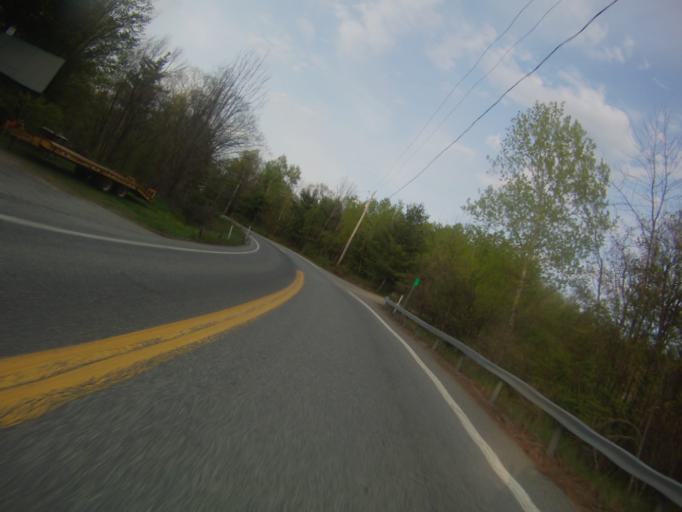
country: US
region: New York
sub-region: Essex County
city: Ticonderoga
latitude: 43.7546
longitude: -73.5535
